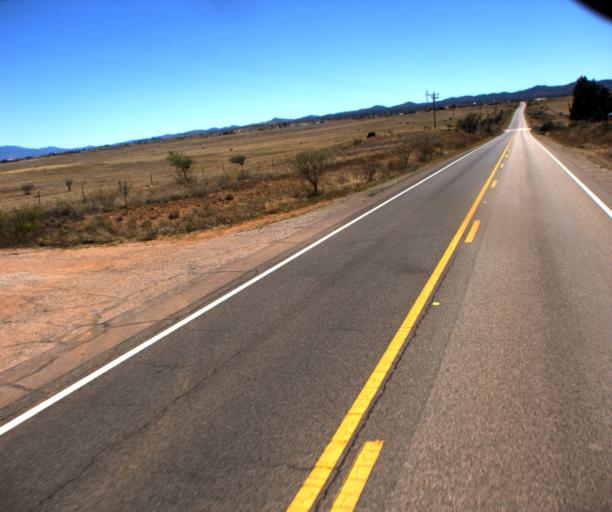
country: US
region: Arizona
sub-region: Pima County
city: Corona de Tucson
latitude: 31.6952
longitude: -110.6555
